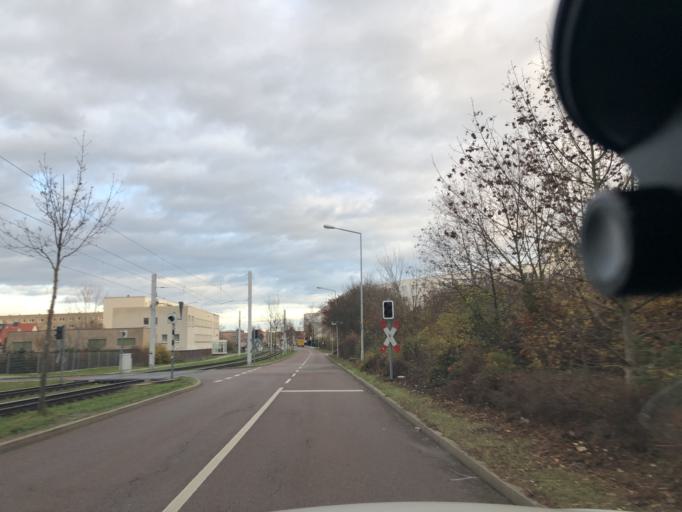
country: DE
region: Saxony-Anhalt
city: Halle Neustadt
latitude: 51.4795
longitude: 11.8958
